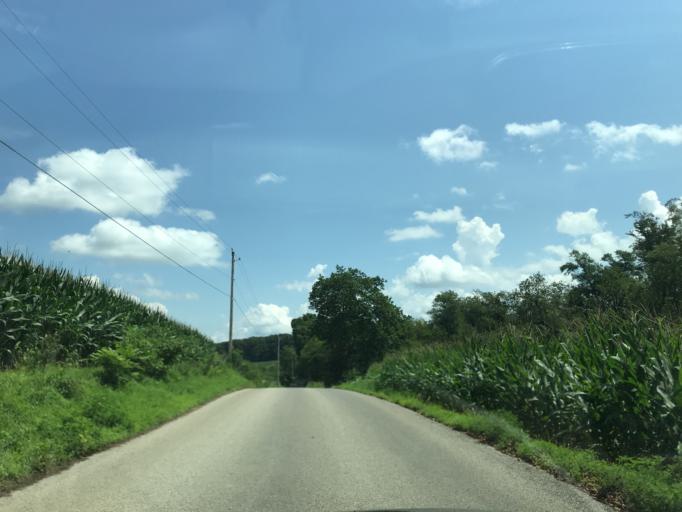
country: US
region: Pennsylvania
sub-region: York County
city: New Freedom
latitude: 39.7210
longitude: -76.7157
